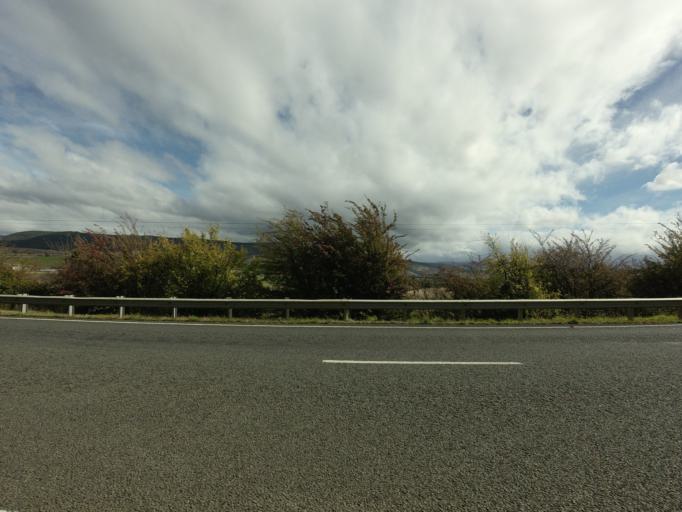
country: AU
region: Tasmania
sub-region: Derwent Valley
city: New Norfolk
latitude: -42.7167
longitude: 146.9477
